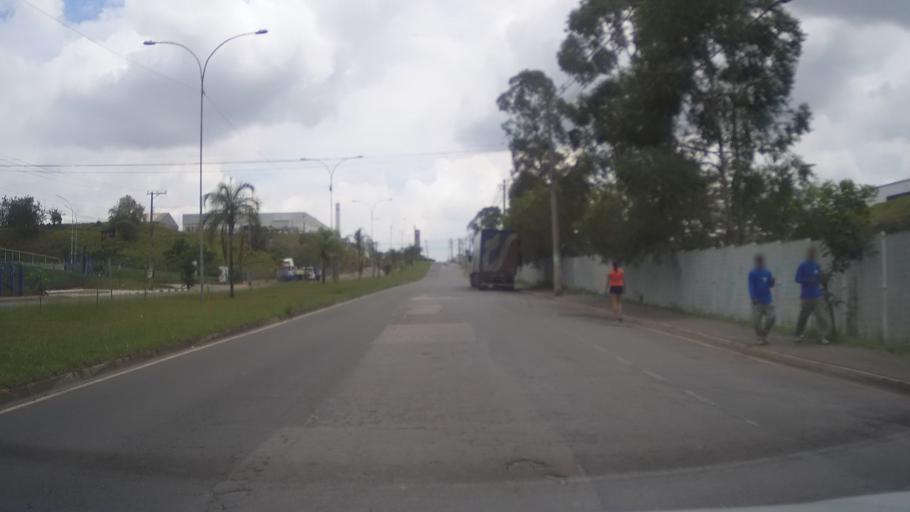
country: BR
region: Sao Paulo
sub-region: Itupeva
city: Itupeva
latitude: -23.1625
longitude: -47.0042
